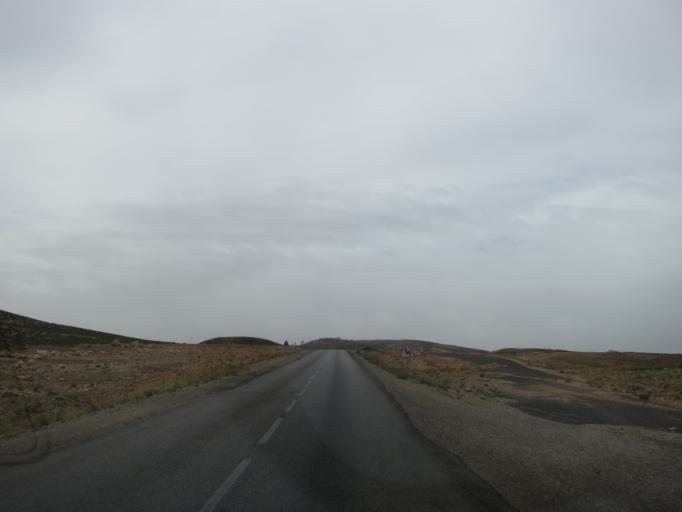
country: MA
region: Meknes-Tafilalet
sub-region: Khenifra
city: Itzer
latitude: 33.1187
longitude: -5.0302
